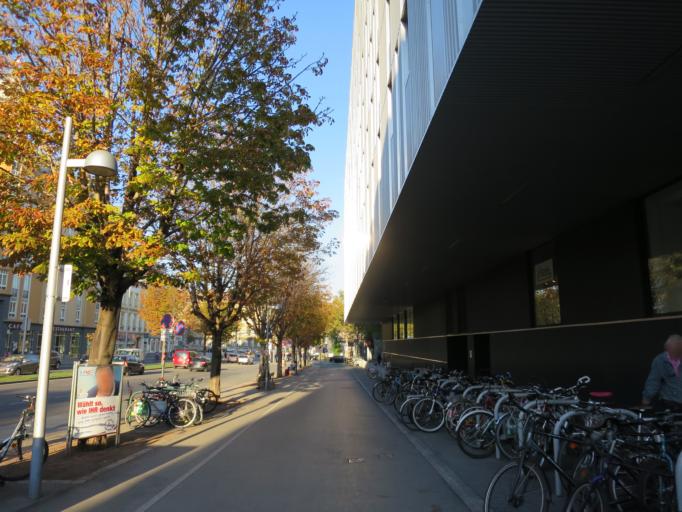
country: AT
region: Vienna
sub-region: Wien Stadt
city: Vienna
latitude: 48.1977
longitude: 16.3370
